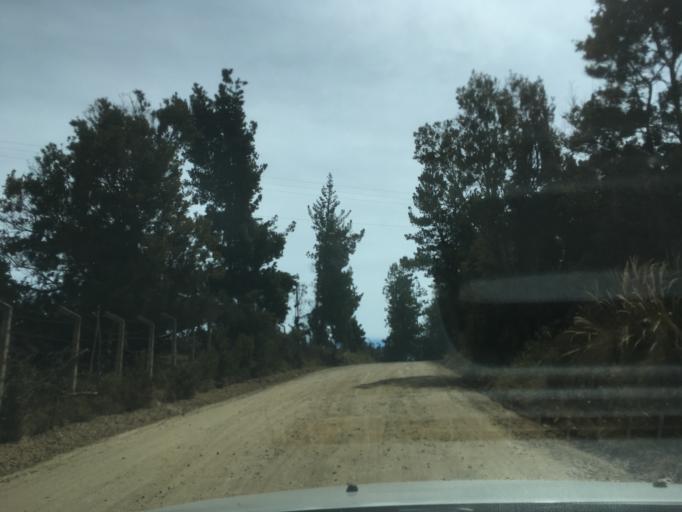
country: CO
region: Boyaca
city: Aquitania
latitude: 5.5733
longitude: -72.9465
